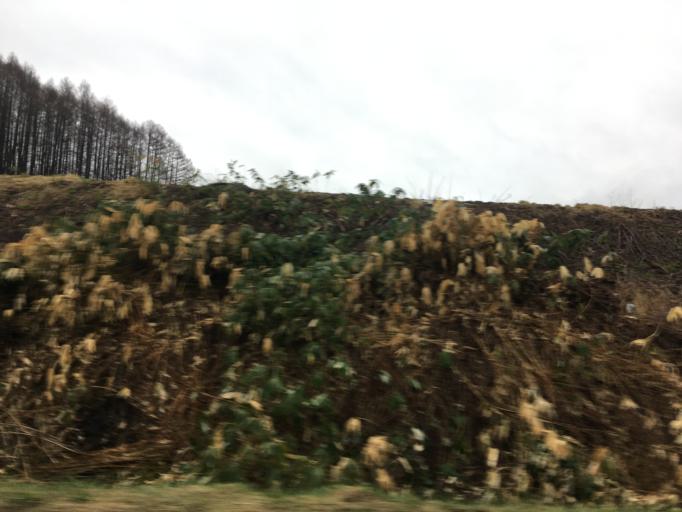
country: JP
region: Hokkaido
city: Nayoro
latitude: 44.0723
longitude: 142.4136
